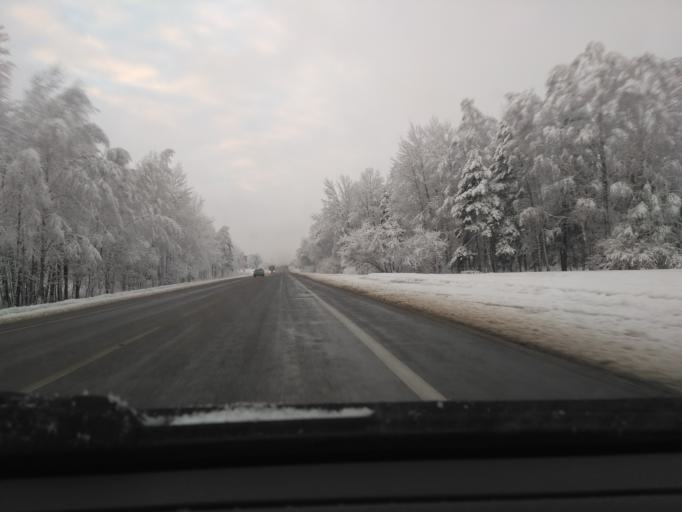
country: BY
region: Minsk
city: Horad Zhodzina
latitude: 54.1216
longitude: 28.3593
